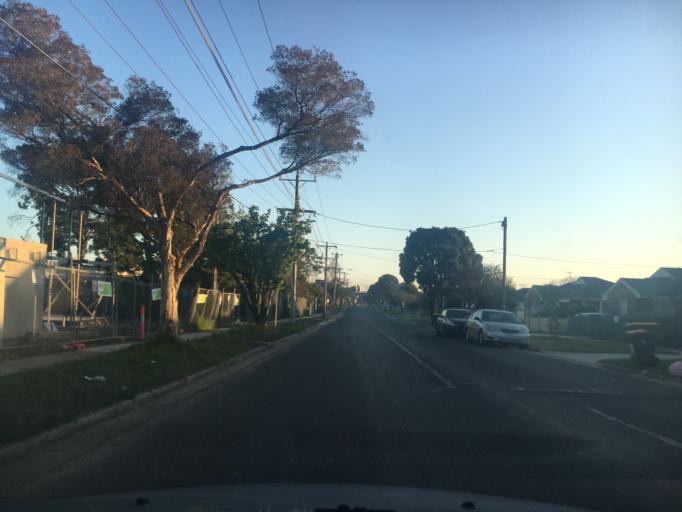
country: AU
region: Victoria
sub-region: Monash
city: Clayton
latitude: -37.9244
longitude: 145.1268
